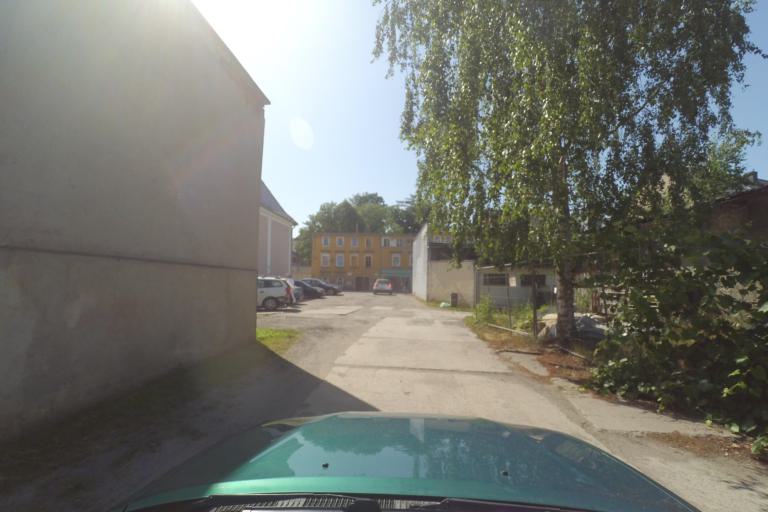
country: PL
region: Lower Silesian Voivodeship
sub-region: Powiat lwowecki
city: Lwowek Slaski
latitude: 51.1129
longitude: 15.5873
